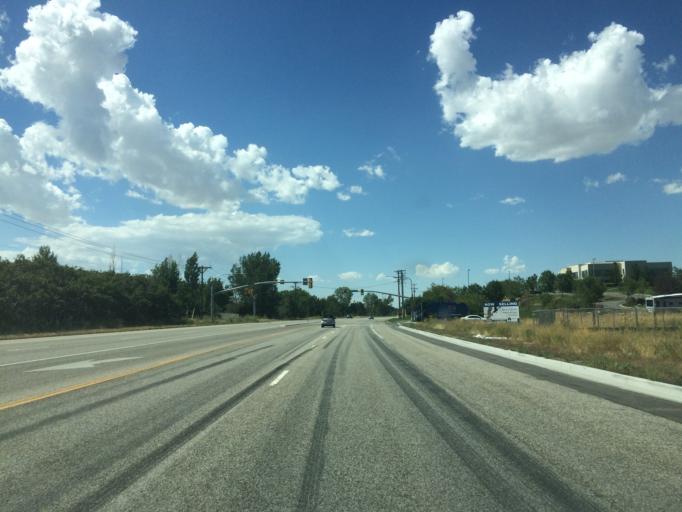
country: US
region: Utah
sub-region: Davis County
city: South Weber
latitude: 41.1022
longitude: -111.9315
